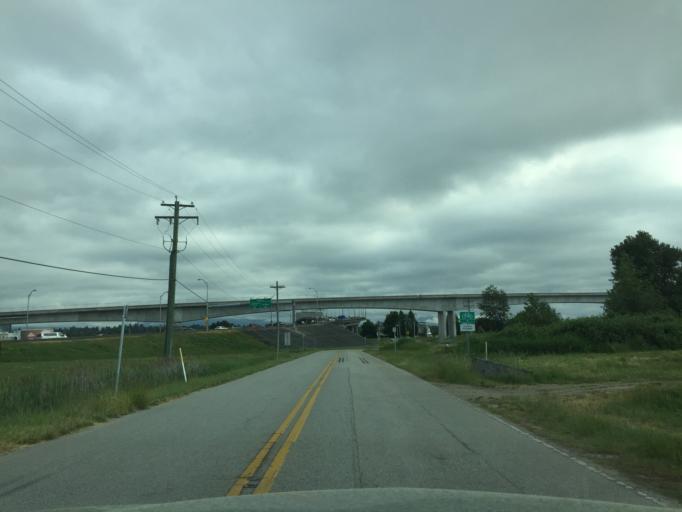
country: CA
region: British Columbia
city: Richmond
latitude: 49.1942
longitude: -123.1387
